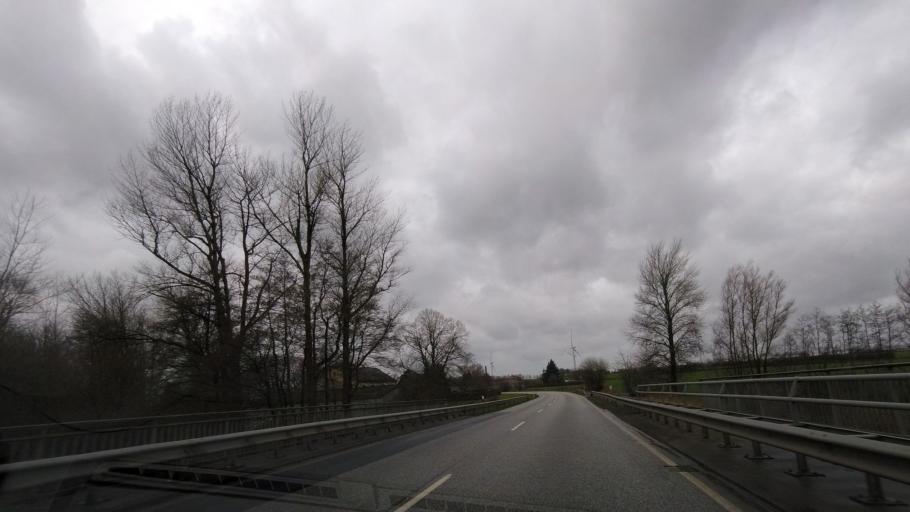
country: DE
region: Schleswig-Holstein
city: Twedt
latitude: 54.6038
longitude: 9.6882
